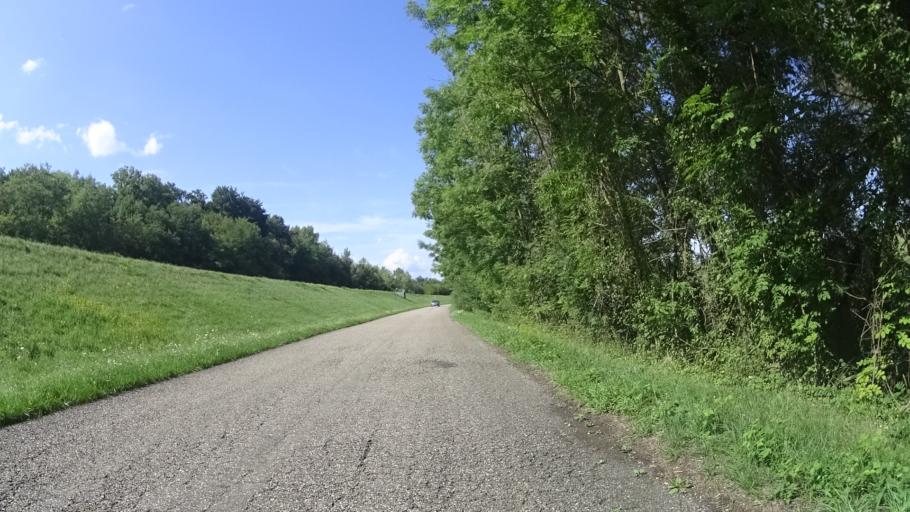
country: DE
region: Baden-Wuerttemberg
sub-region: Karlsruhe Region
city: Hugelsheim
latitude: 48.8311
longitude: 8.1008
